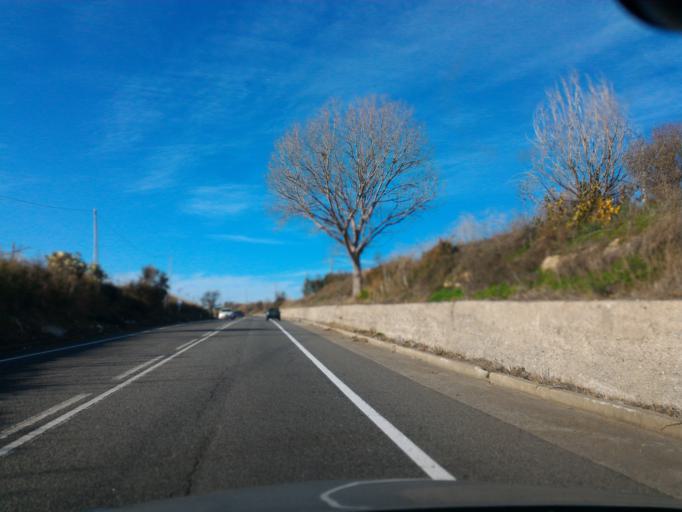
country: IT
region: Calabria
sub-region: Provincia di Crotone
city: Isola di Capo Rizzuto
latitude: 38.9389
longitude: 17.0661
